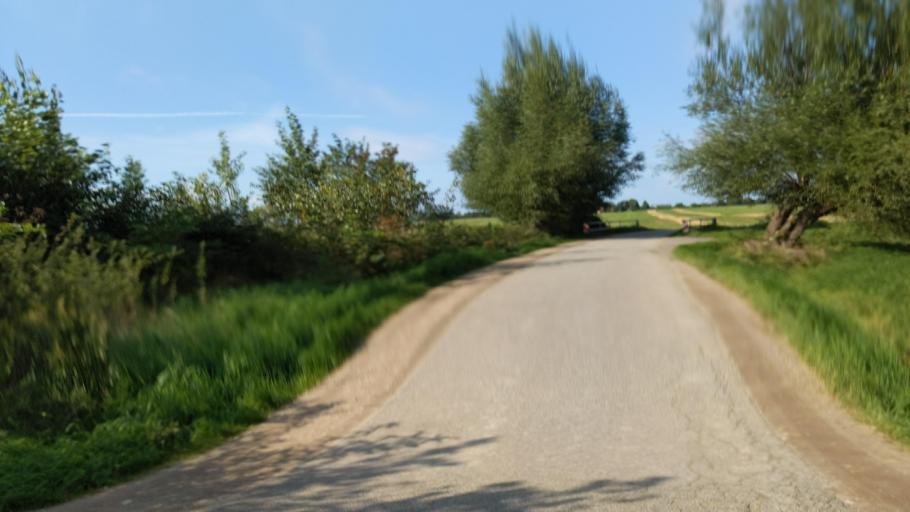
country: DE
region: Mecklenburg-Vorpommern
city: Kalkhorst
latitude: 53.9600
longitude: 10.9992
